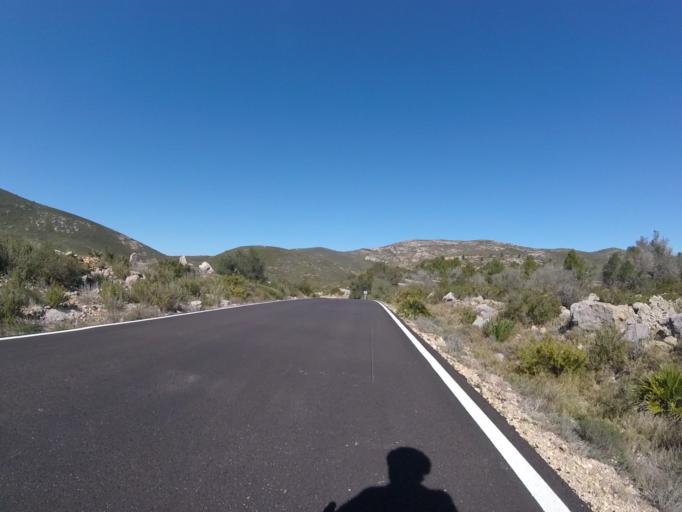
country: ES
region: Valencia
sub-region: Provincia de Castello
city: Cervera del Maestre
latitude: 40.4021
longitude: 0.2305
